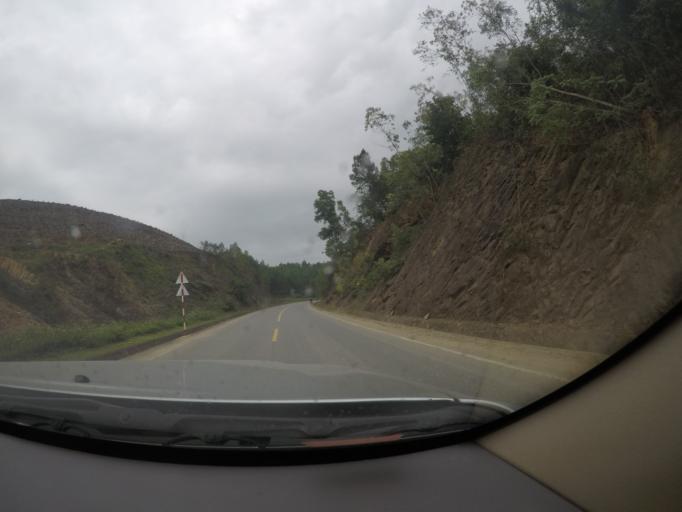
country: VN
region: Quang Binh
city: Ba Don
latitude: 17.6176
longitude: 106.3752
